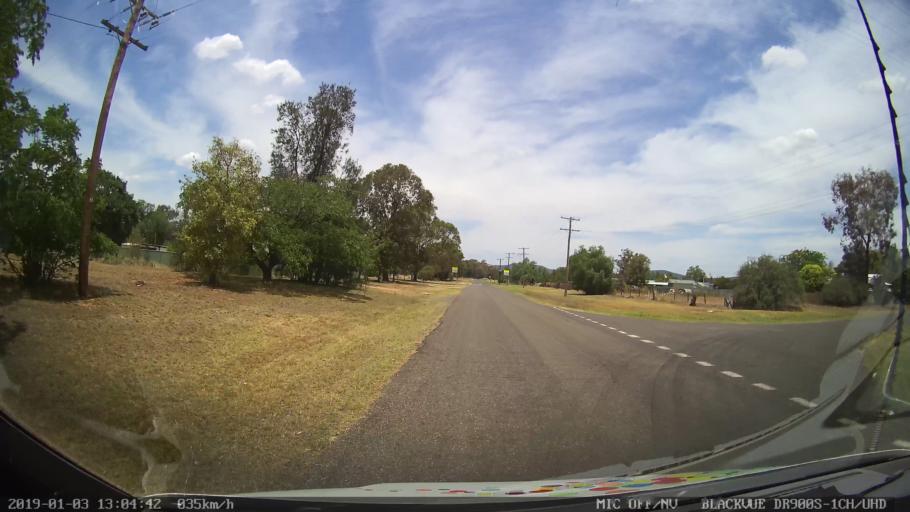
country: AU
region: New South Wales
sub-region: Cabonne
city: Canowindra
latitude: -33.6145
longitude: 148.4381
